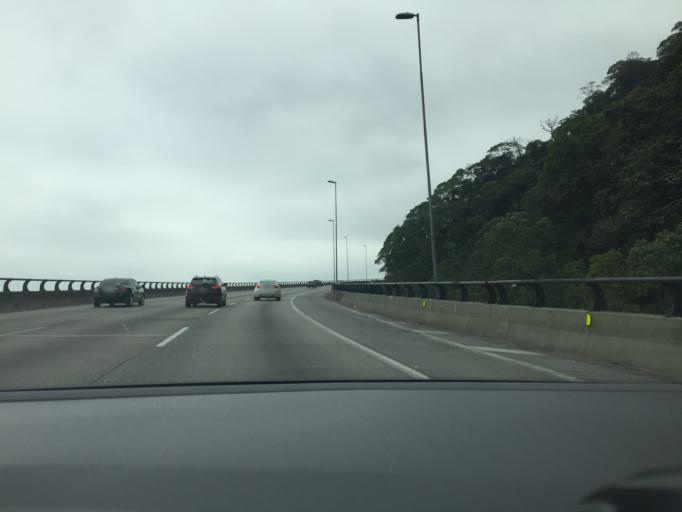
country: BR
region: Sao Paulo
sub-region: Cubatao
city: Cubatao
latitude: -23.9066
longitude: -46.5066
